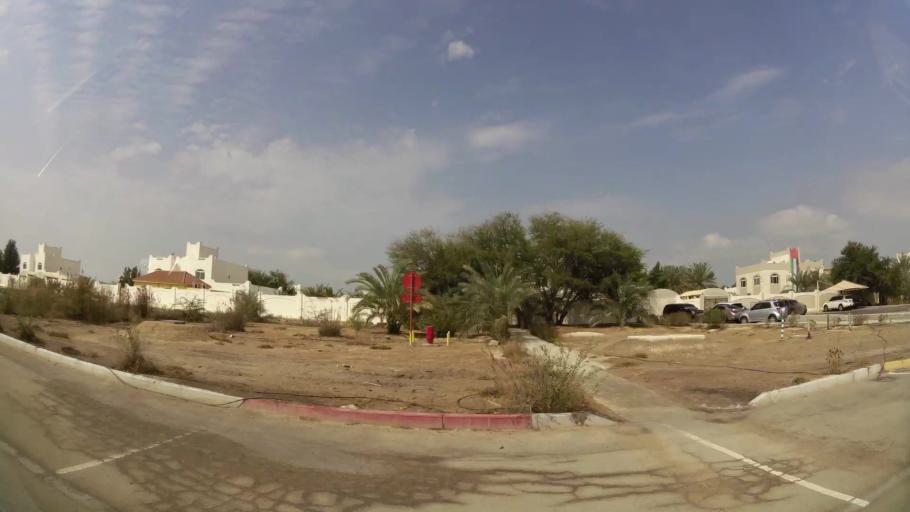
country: AE
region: Abu Dhabi
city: Abu Dhabi
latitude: 24.5533
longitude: 54.6396
